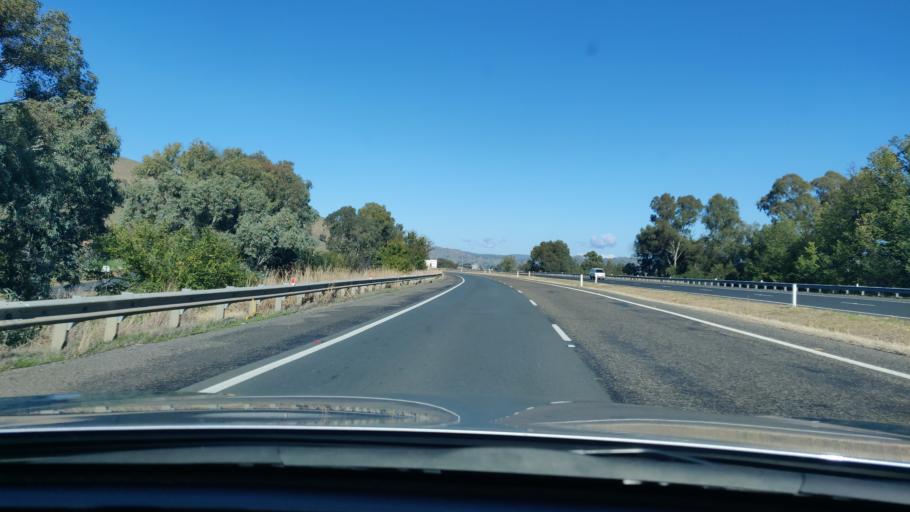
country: AU
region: New South Wales
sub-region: Gundagai
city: Gundagai
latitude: -35.0926
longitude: 148.0757
